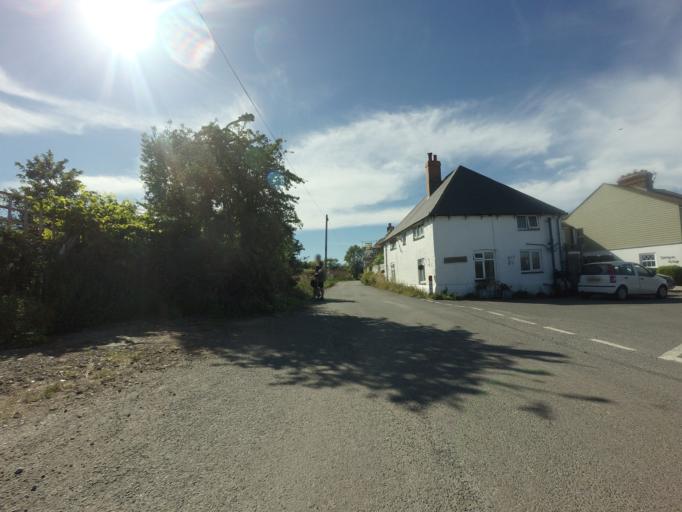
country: GB
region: England
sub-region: Kent
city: Birchington-on-Sea
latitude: 51.3612
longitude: 1.2431
